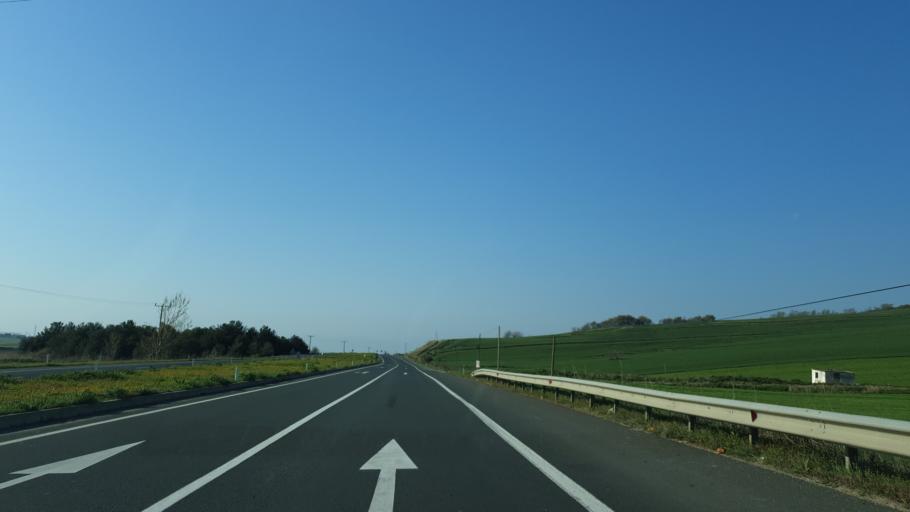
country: TR
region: Tekirdag
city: Corlu
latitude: 41.0484
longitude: 27.7339
